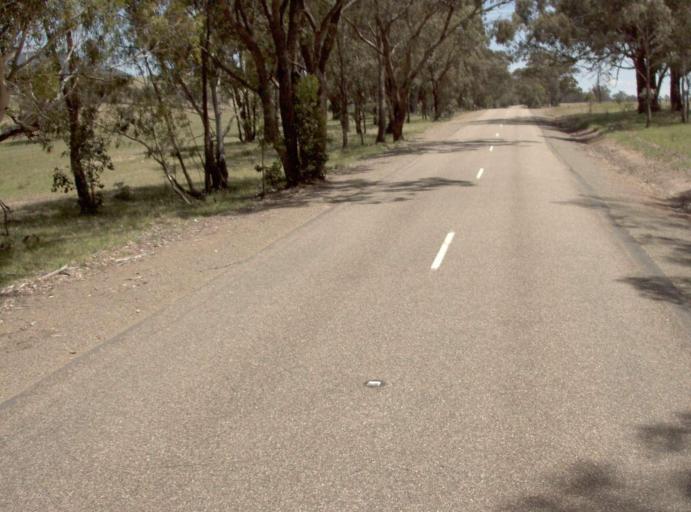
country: AU
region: Victoria
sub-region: East Gippsland
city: Bairnsdale
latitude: -37.3397
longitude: 147.7911
